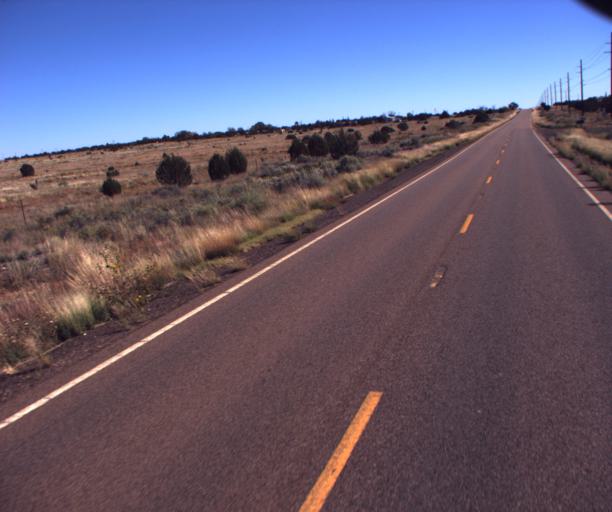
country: US
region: Arizona
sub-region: Navajo County
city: Taylor
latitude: 34.4839
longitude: -110.2602
